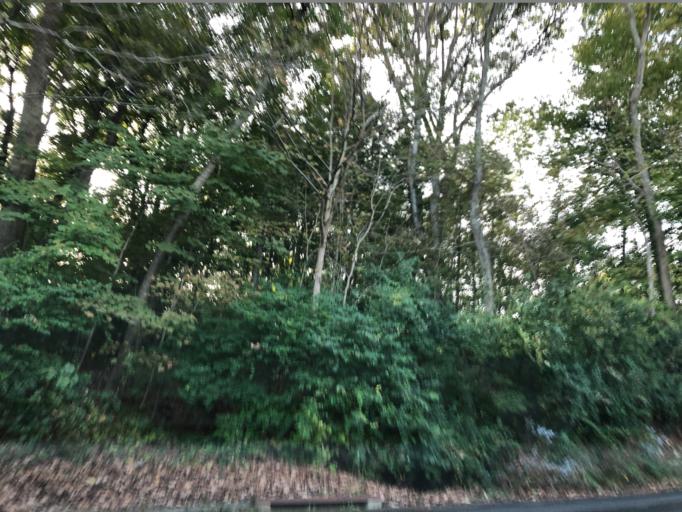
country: US
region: Ohio
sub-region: Warren County
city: Loveland Park
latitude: 39.2850
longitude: -84.2660
